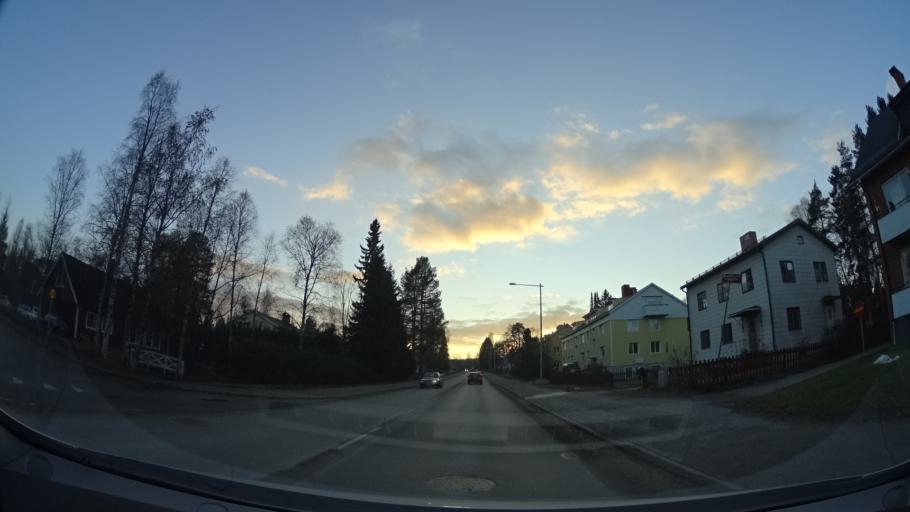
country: SE
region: Vaesterbotten
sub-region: Lycksele Kommun
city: Lycksele
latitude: 64.5906
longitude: 18.6710
